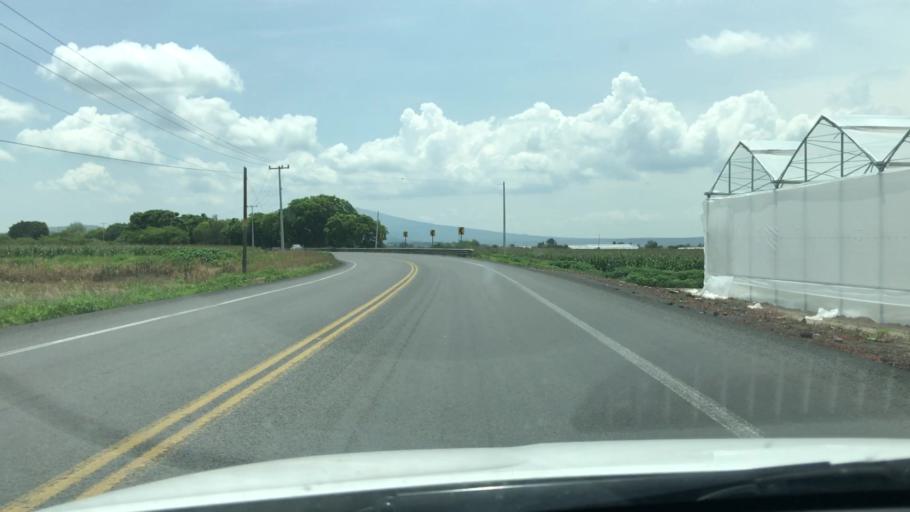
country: MX
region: Michoacan
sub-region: Yurecuaro
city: Yurecuaro
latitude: 20.3190
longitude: -102.2986
